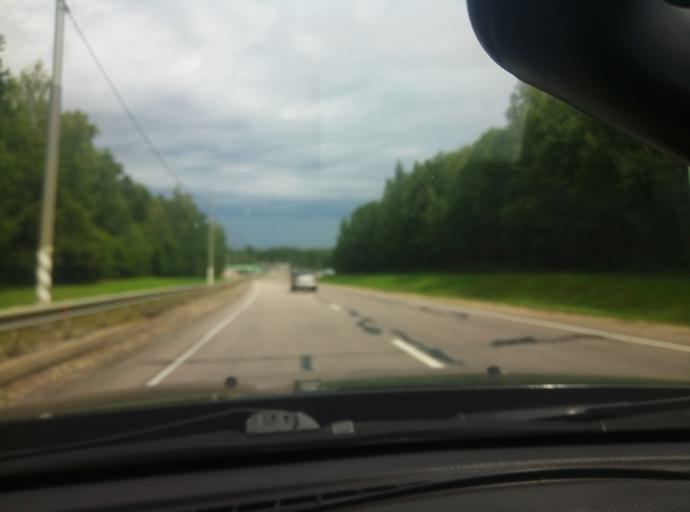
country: RU
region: Tula
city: Leninskiy
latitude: 54.4110
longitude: 37.5017
